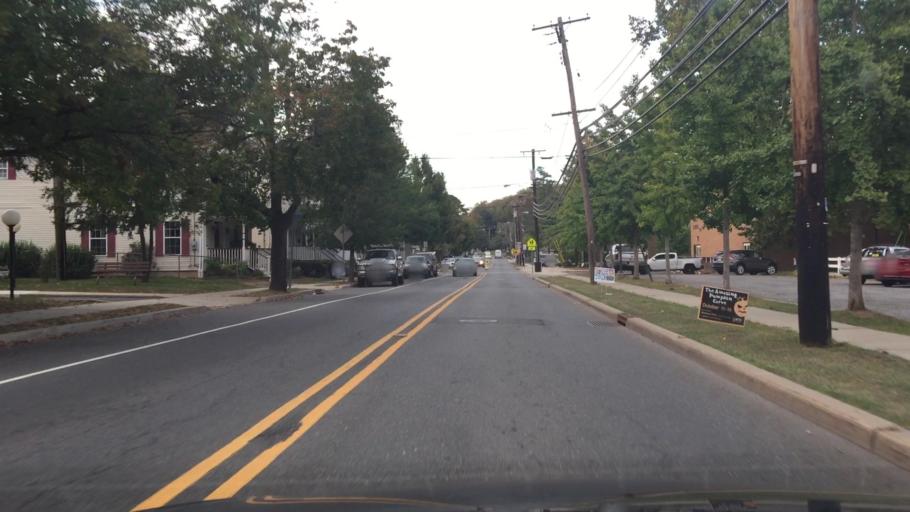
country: US
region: New Jersey
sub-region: Hunterdon County
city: Lambertville
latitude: 40.3725
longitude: -74.9447
